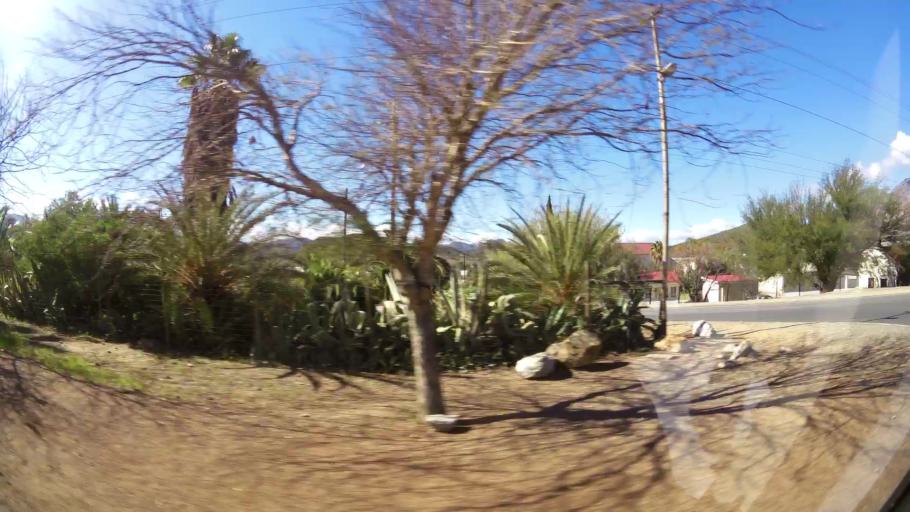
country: ZA
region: Western Cape
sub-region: Cape Winelands District Municipality
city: Ashton
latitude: -33.7760
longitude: 20.1322
